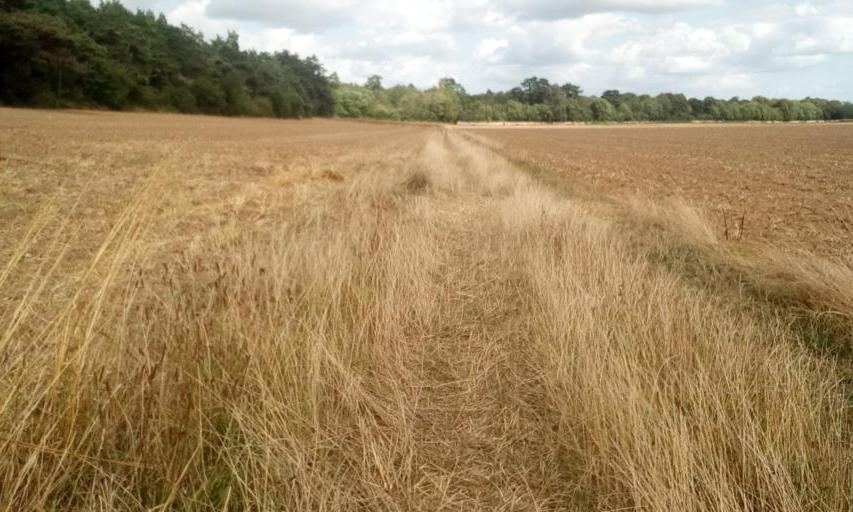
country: FR
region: Lower Normandy
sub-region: Departement du Calvados
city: Bellengreville
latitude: 49.1123
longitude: -0.2400
